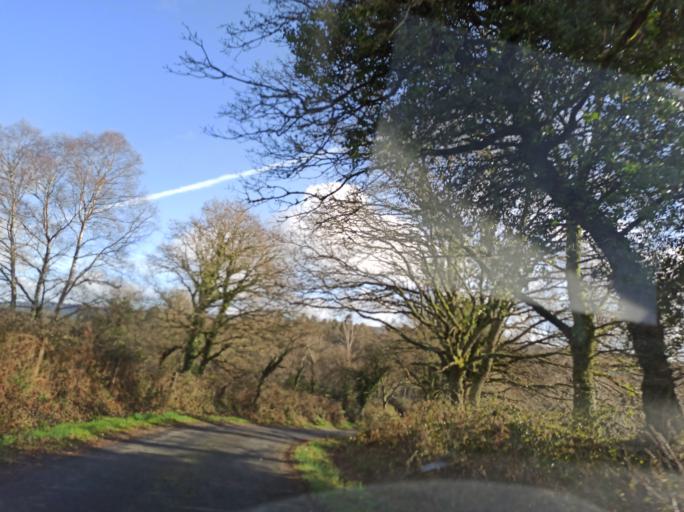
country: ES
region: Galicia
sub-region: Provincia da Coruna
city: Sobrado
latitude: 43.0831
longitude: -7.9417
